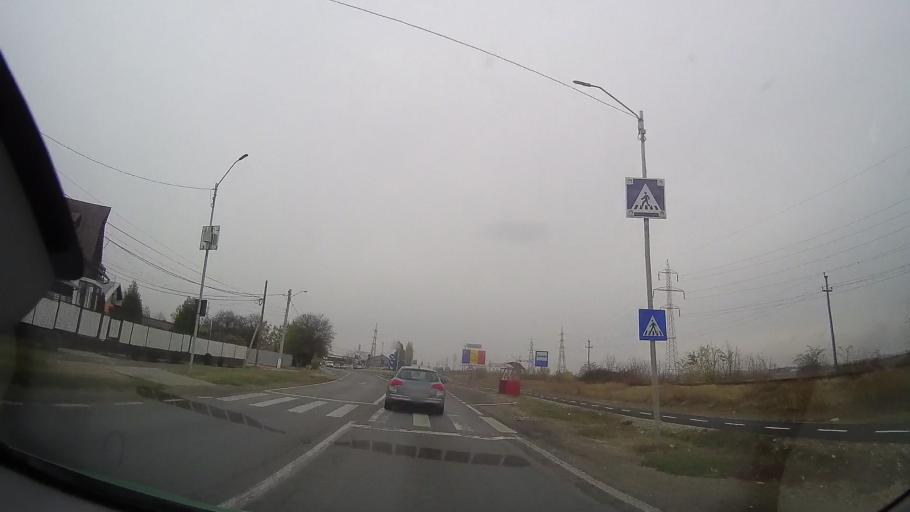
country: RO
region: Prahova
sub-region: Comuna Blejoiu
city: Ploiestiori
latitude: 44.9765
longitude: 26.0174
